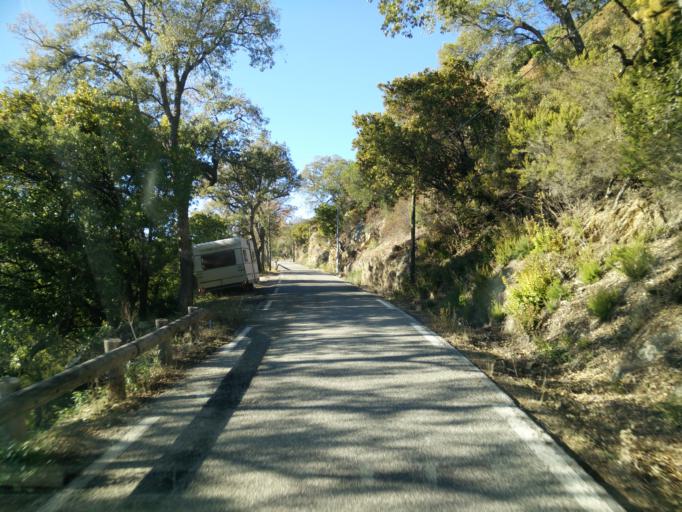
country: FR
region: Provence-Alpes-Cote d'Azur
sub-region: Departement du Var
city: La Garde-Freinet
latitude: 43.2573
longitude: 6.4369
